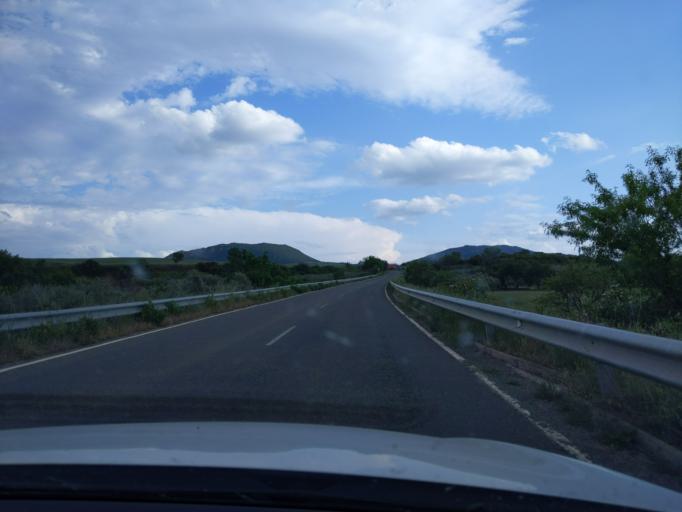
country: ES
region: La Rioja
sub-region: Provincia de La Rioja
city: Alberite
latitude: 42.3860
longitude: -2.4237
